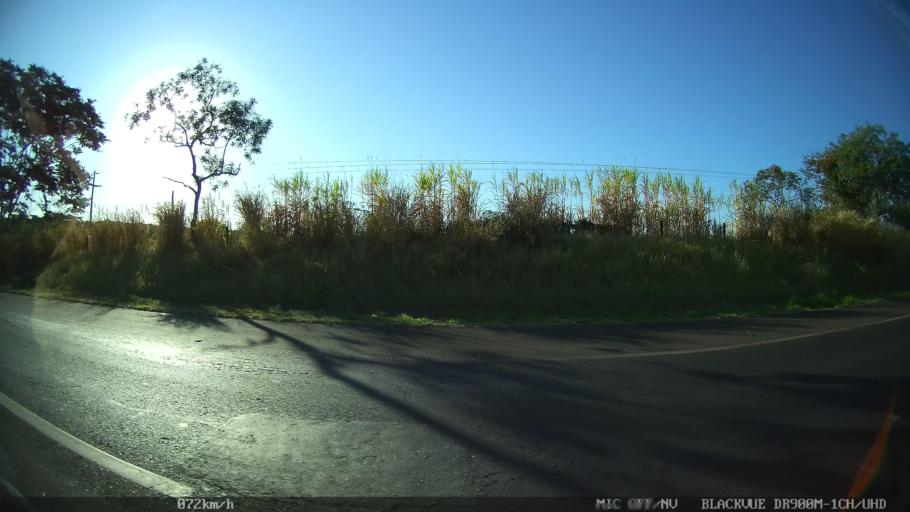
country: BR
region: Sao Paulo
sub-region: Guapiacu
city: Guapiacu
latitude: -20.7832
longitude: -49.2668
